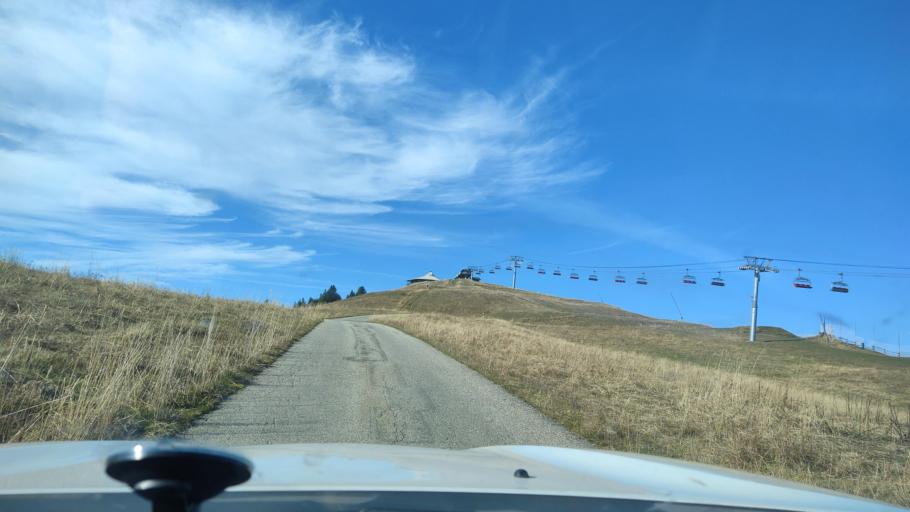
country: FR
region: Rhone-Alpes
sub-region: Departement de la Savoie
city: Beaufort
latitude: 45.7486
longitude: 6.5140
